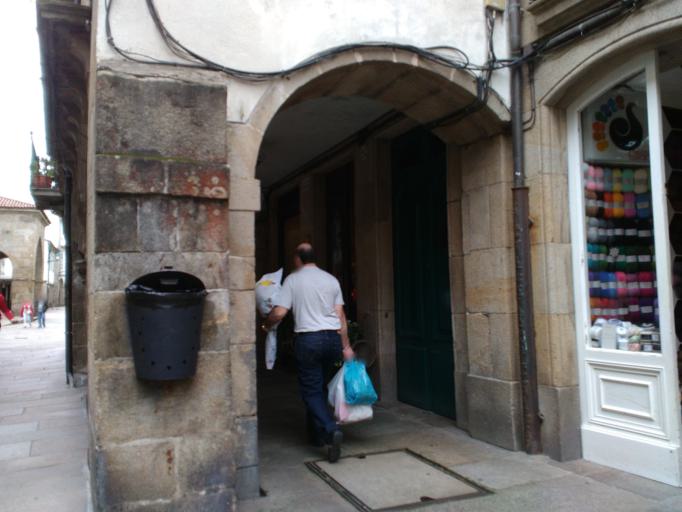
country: ES
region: Galicia
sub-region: Provincia da Coruna
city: Santiago de Compostela
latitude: 42.8789
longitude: -8.5435
